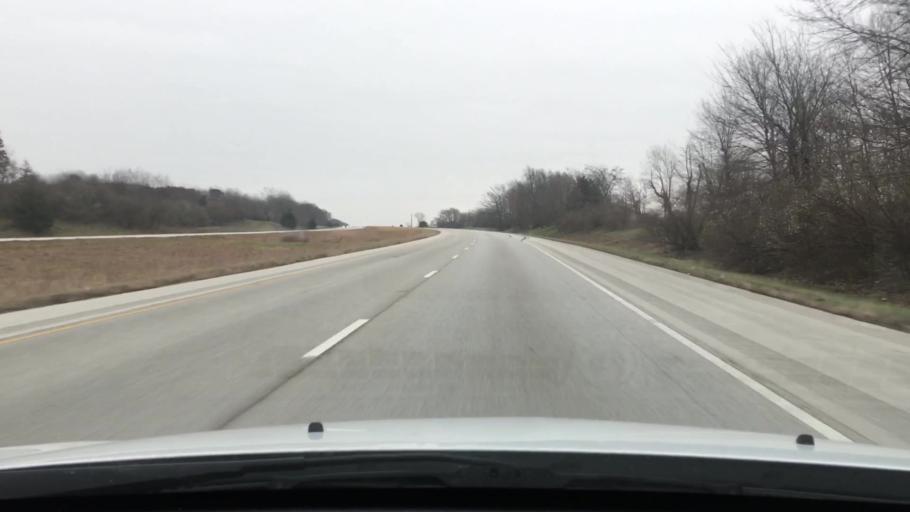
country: US
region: Illinois
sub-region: Scott County
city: Winchester
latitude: 39.6803
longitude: -90.3881
